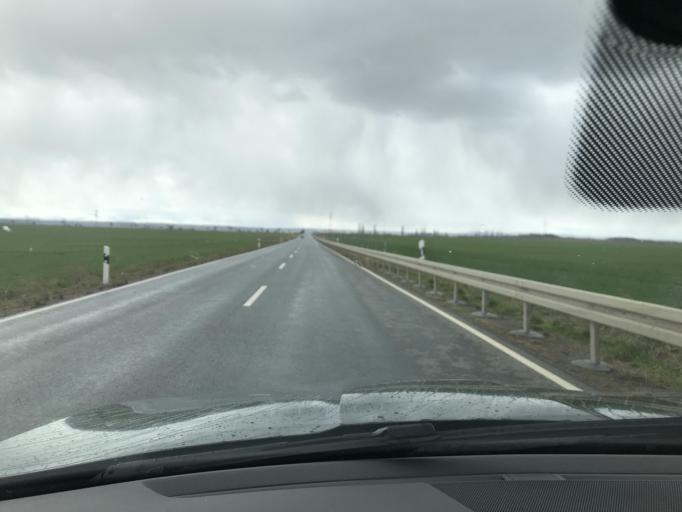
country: DE
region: Saxony-Anhalt
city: Hoym
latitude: 51.7738
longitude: 11.2987
